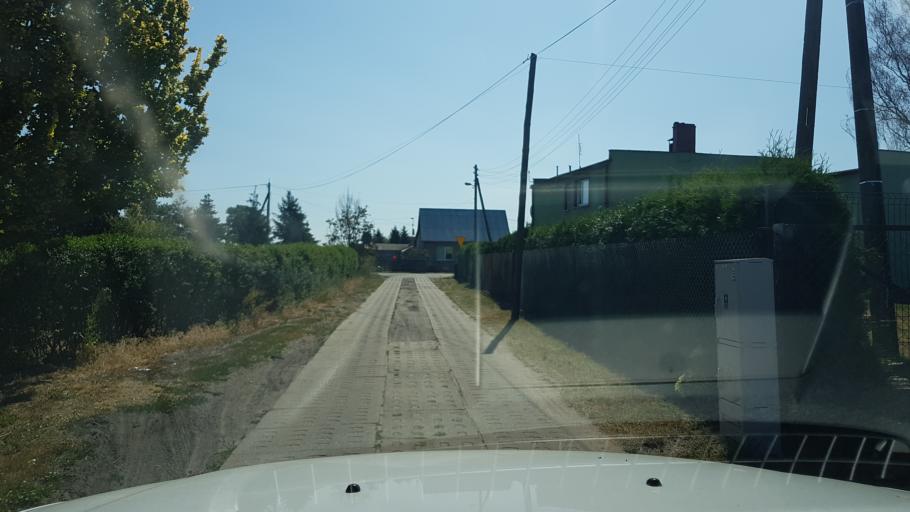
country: PL
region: West Pomeranian Voivodeship
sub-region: Powiat goleniowski
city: Goleniow
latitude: 53.5065
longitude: 14.7094
